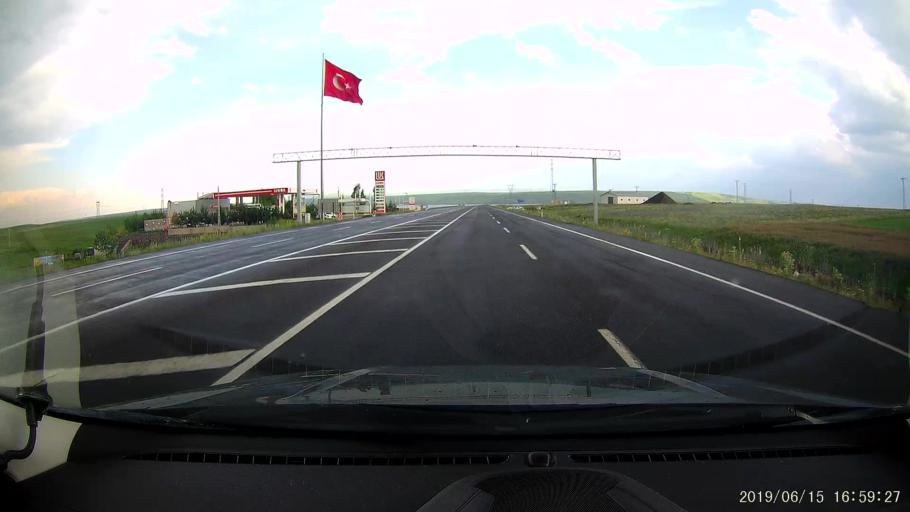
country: TR
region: Kars
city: Susuz
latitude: 40.7519
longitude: 43.1507
